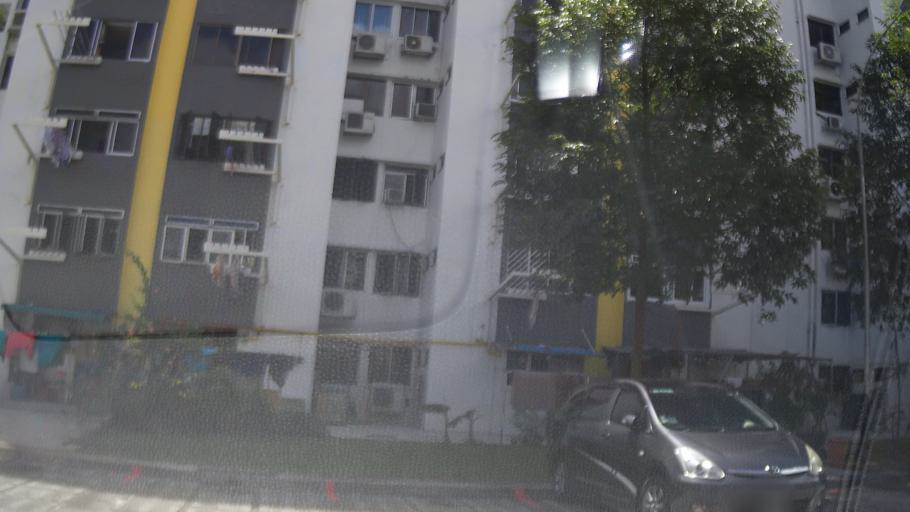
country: SG
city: Singapore
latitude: 1.3230
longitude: 103.8859
